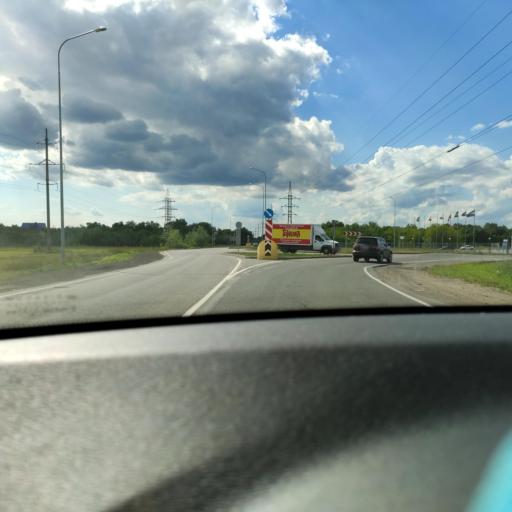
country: RU
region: Samara
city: Samara
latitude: 53.1315
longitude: 50.1400
